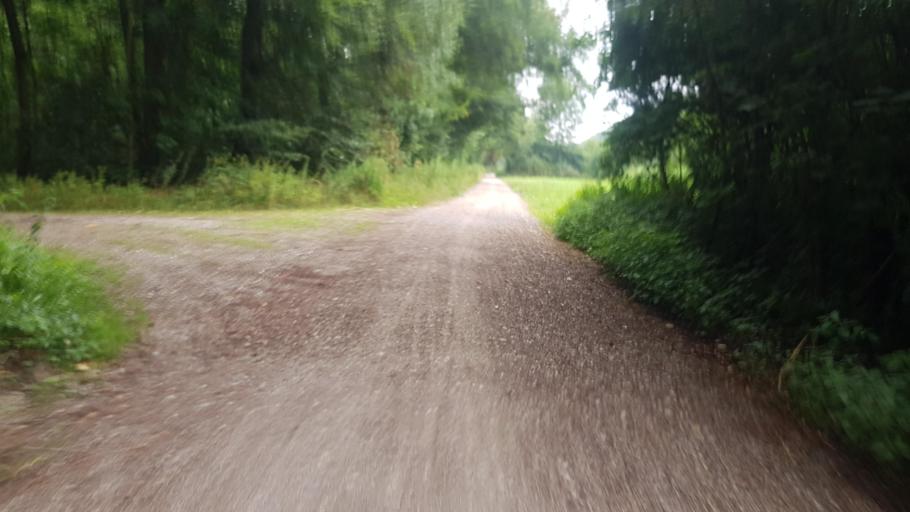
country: DE
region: Bavaria
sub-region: Upper Bavaria
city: Gauting
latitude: 48.0446
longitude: 11.3594
